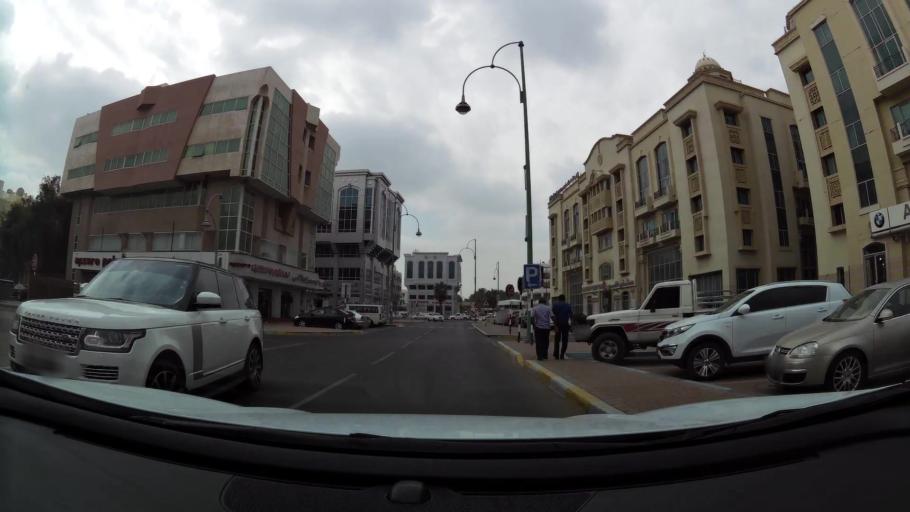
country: AE
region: Abu Dhabi
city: Al Ain
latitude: 24.2233
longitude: 55.7685
